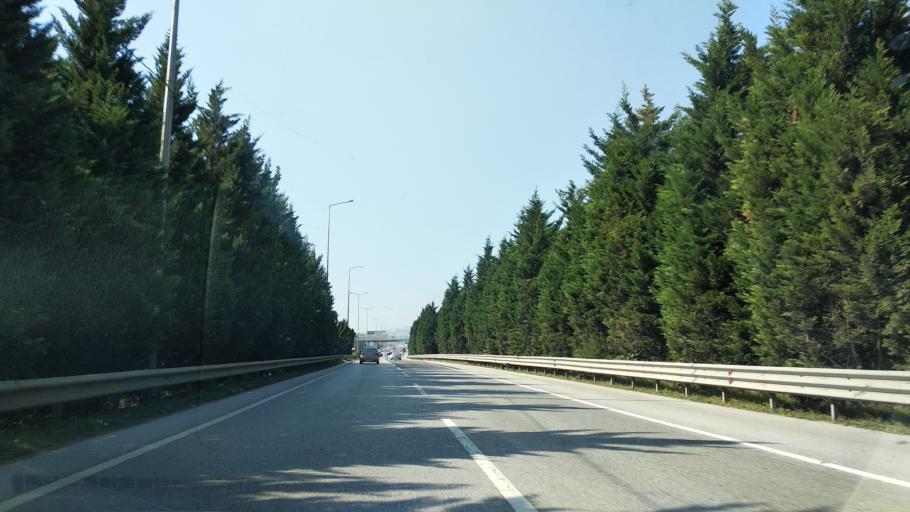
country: TR
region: Kocaeli
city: Kosekoy
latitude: 40.7559
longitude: 30.0068
